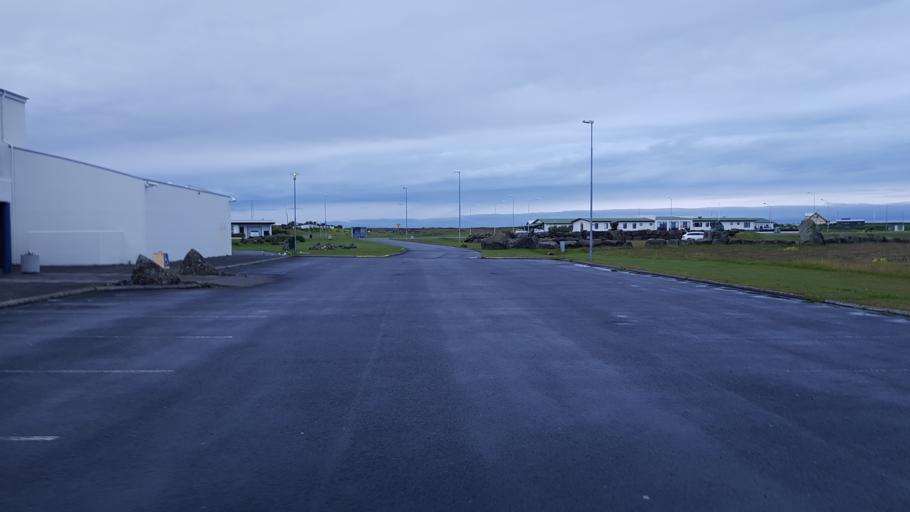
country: IS
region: Southern Peninsula
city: Gardur
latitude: 64.0731
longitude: -22.6555
